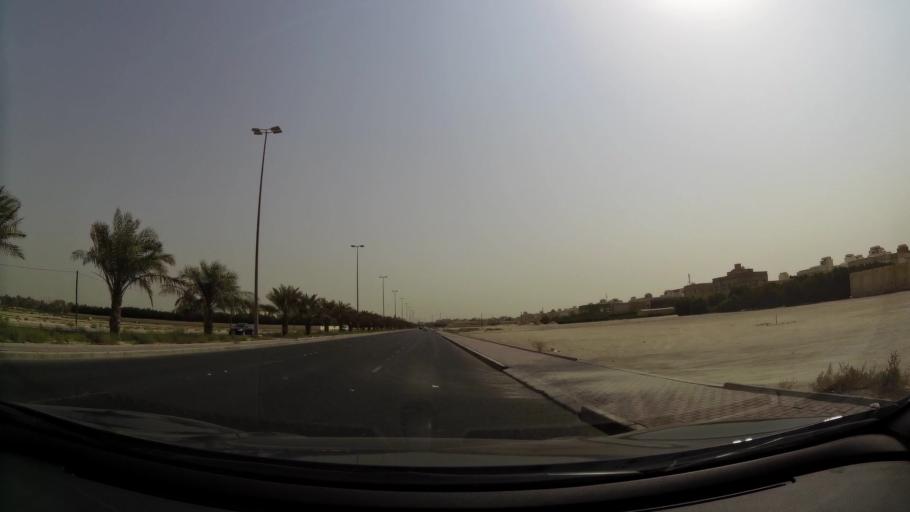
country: KW
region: Muhafazat al Jahra'
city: Al Jahra'
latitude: 29.3247
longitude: 47.7261
